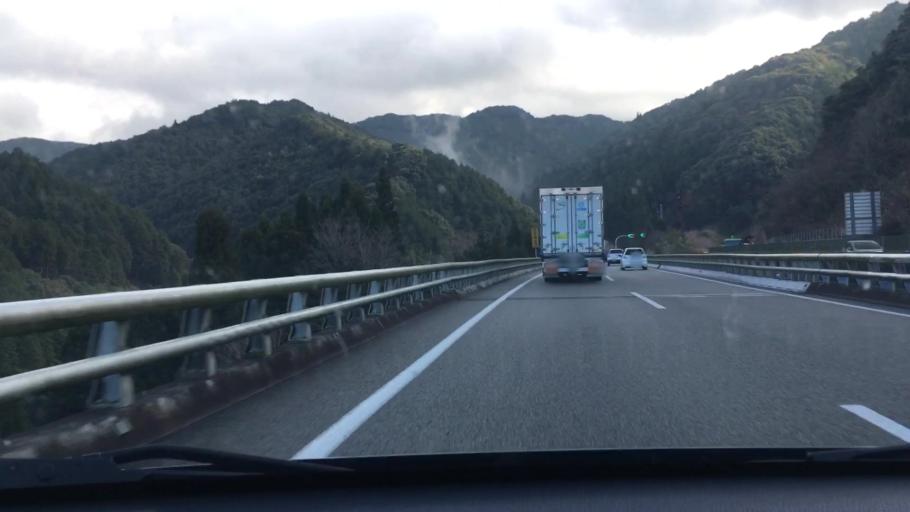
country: JP
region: Kumamoto
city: Hitoyoshi
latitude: 32.1371
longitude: 130.8028
